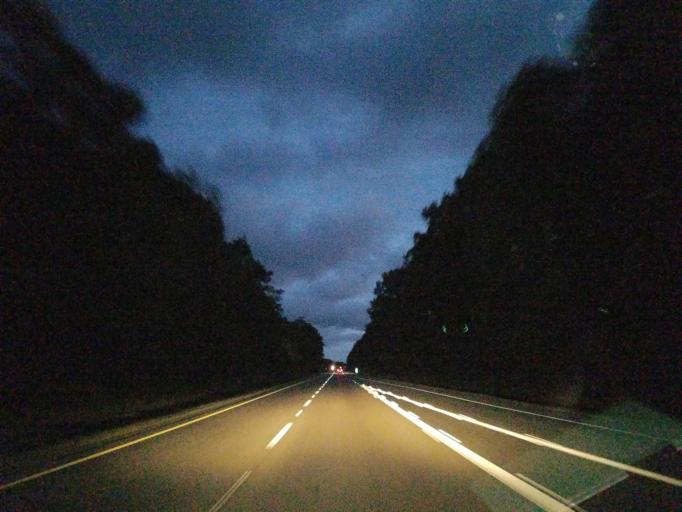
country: US
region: Mississippi
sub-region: Jones County
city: Sharon
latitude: 31.8481
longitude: -89.0493
